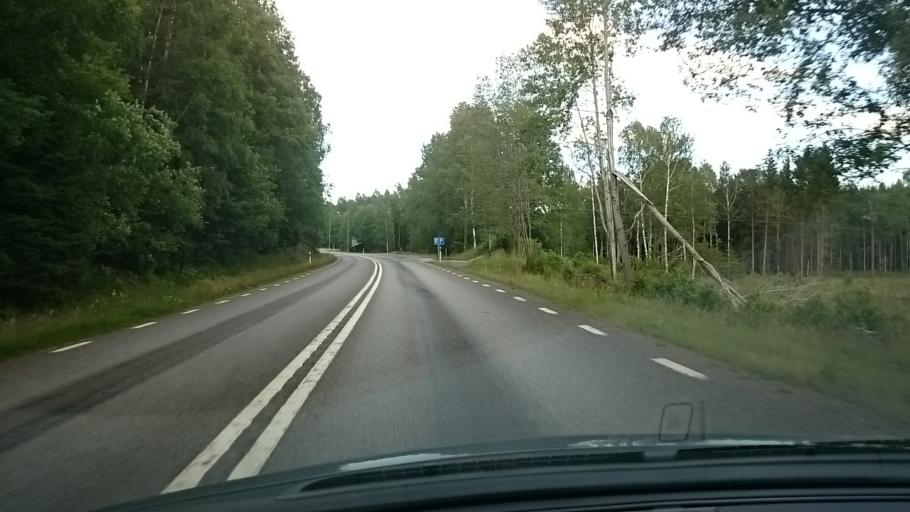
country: SE
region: OErebro
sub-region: Askersunds Kommun
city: Askersund
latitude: 58.7470
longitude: 14.7874
